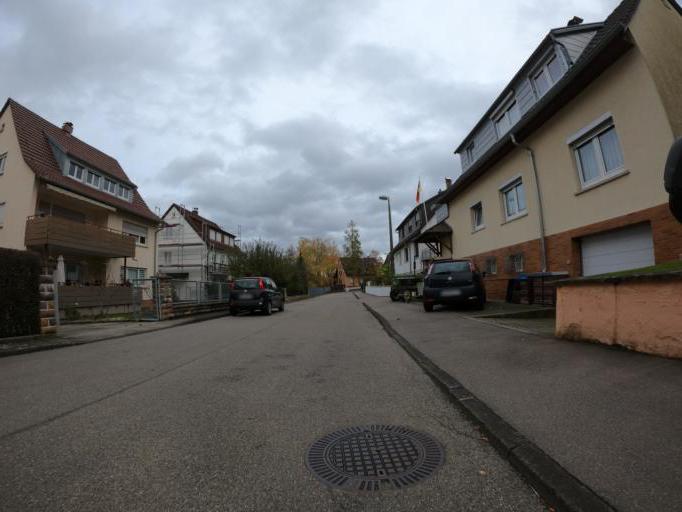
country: DE
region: Baden-Wuerttemberg
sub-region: Regierungsbezirk Stuttgart
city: Ehningen
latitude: 48.6935
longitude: 8.9396
